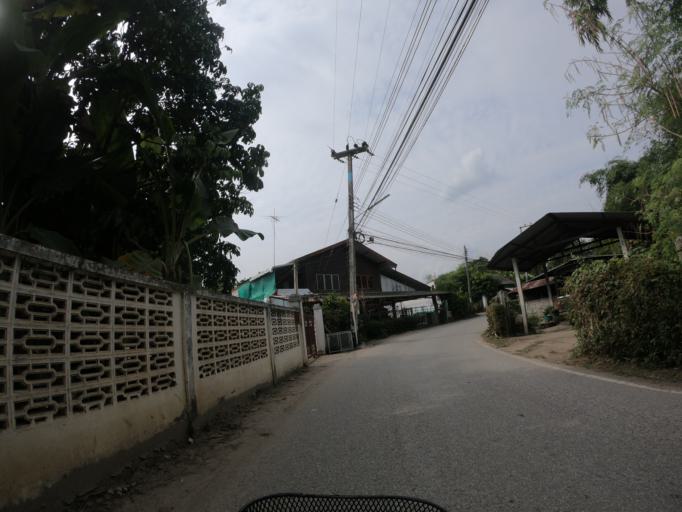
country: TH
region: Chiang Mai
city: Saraphi
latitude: 18.7364
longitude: 99.0250
